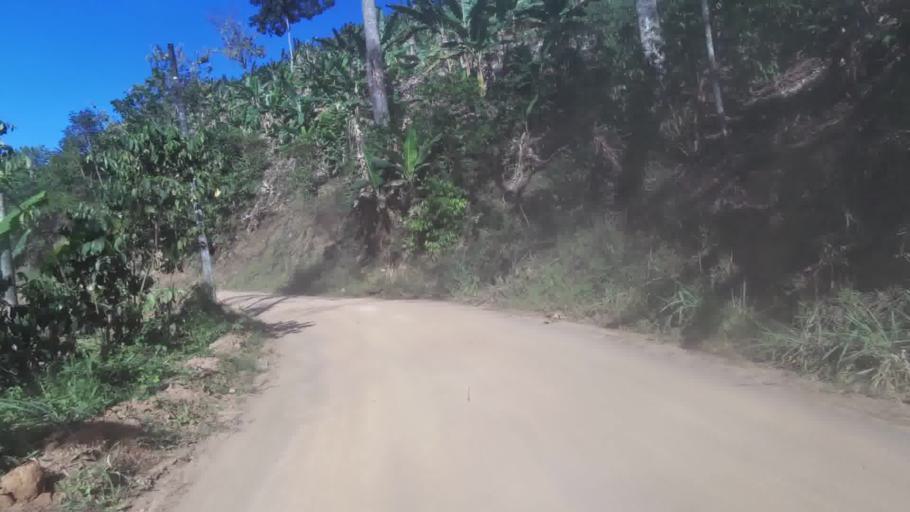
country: BR
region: Espirito Santo
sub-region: Iconha
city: Iconha
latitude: -20.7596
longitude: -40.8207
